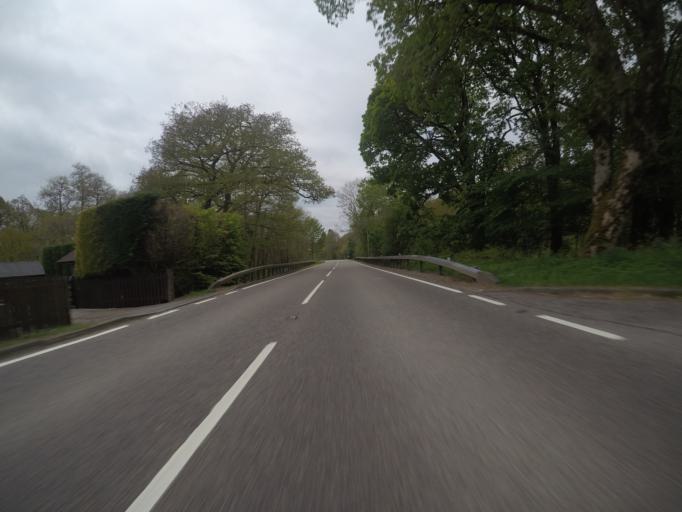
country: GB
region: Scotland
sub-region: Highland
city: Spean Bridge
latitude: 56.8953
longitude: -4.9022
